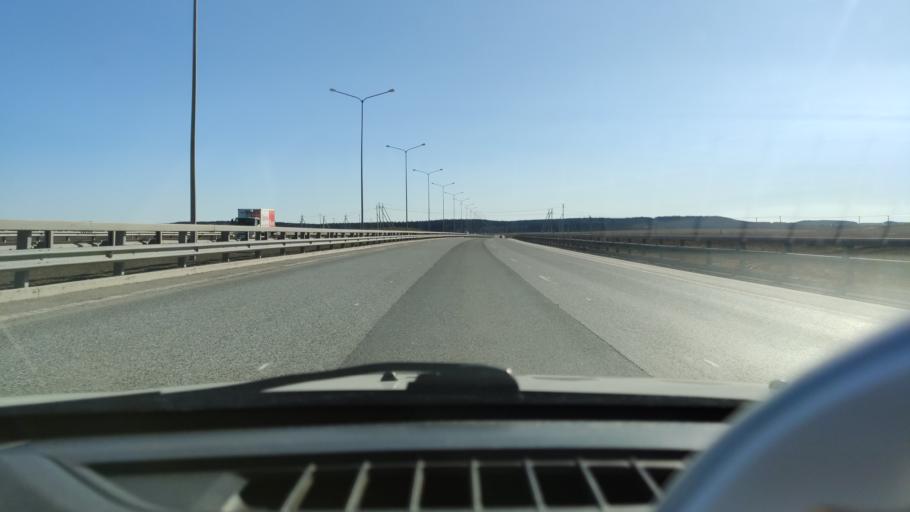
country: RU
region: Perm
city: Lobanovo
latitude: 57.8771
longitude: 56.2652
